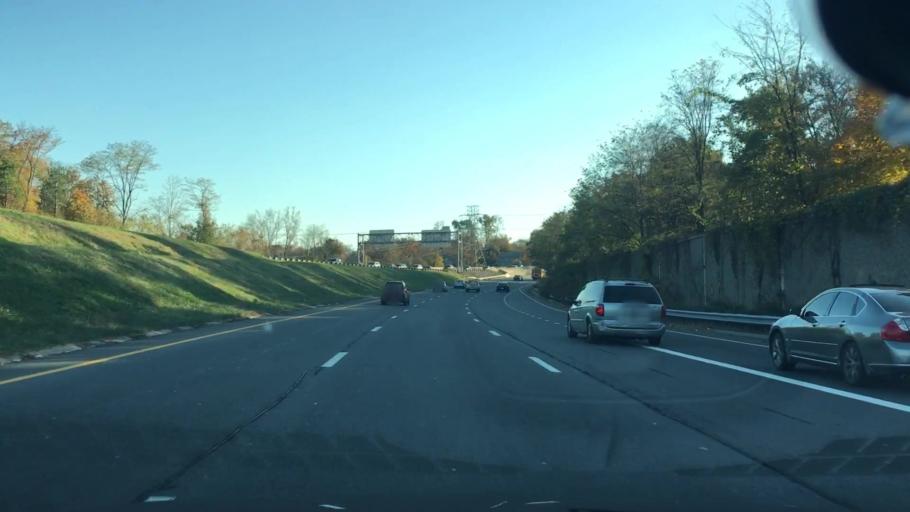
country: US
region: New York
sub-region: Westchester County
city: Elmsford
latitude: 41.0526
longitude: -73.8105
